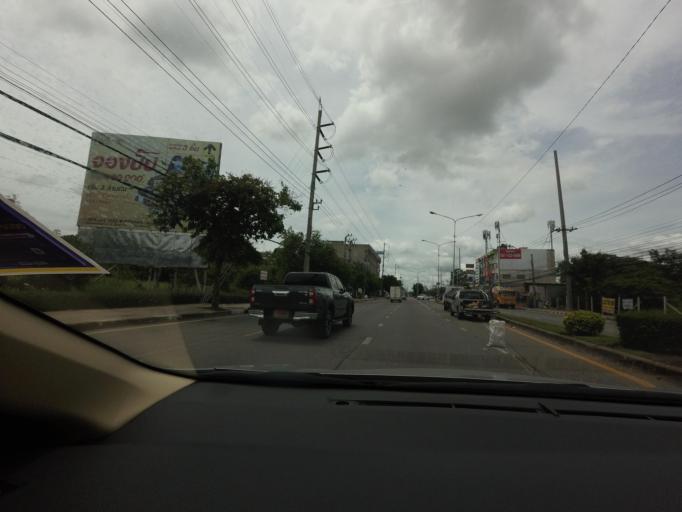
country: TH
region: Bangkok
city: Lat Krabang
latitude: 13.7157
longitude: 100.8079
